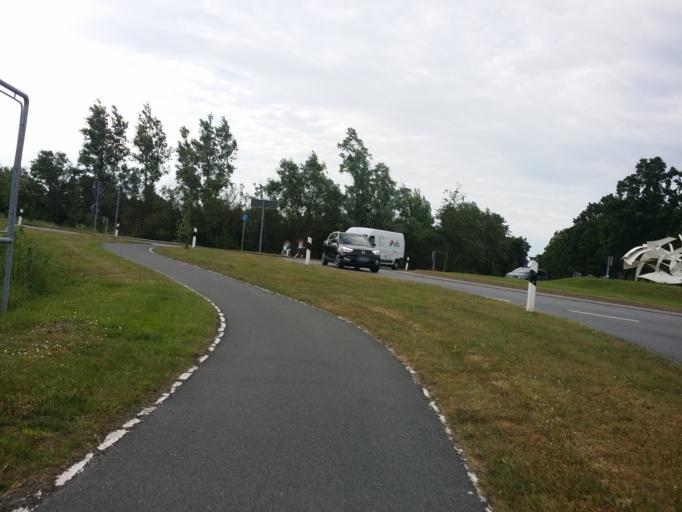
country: DE
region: Lower Saxony
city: Wittmund
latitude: 53.5850
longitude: 7.7828
